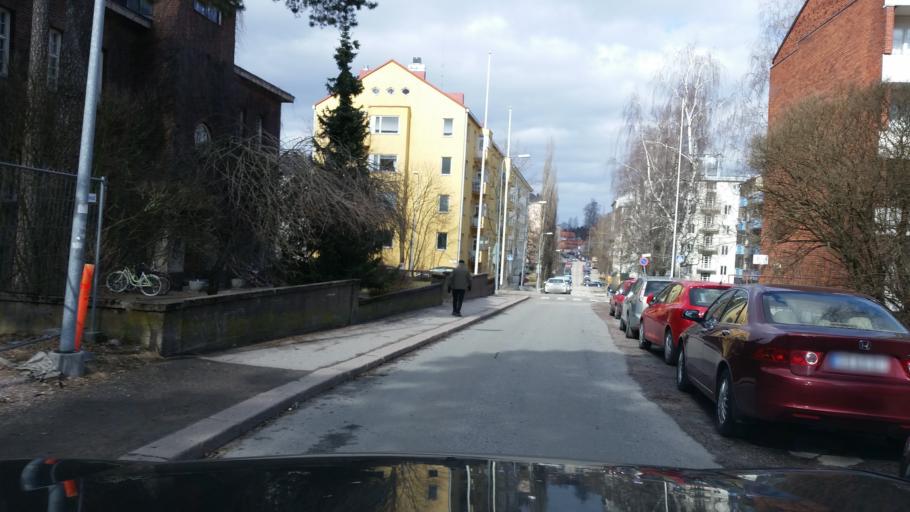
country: FI
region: Uusimaa
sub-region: Helsinki
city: Teekkarikylae
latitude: 60.1961
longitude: 24.8780
